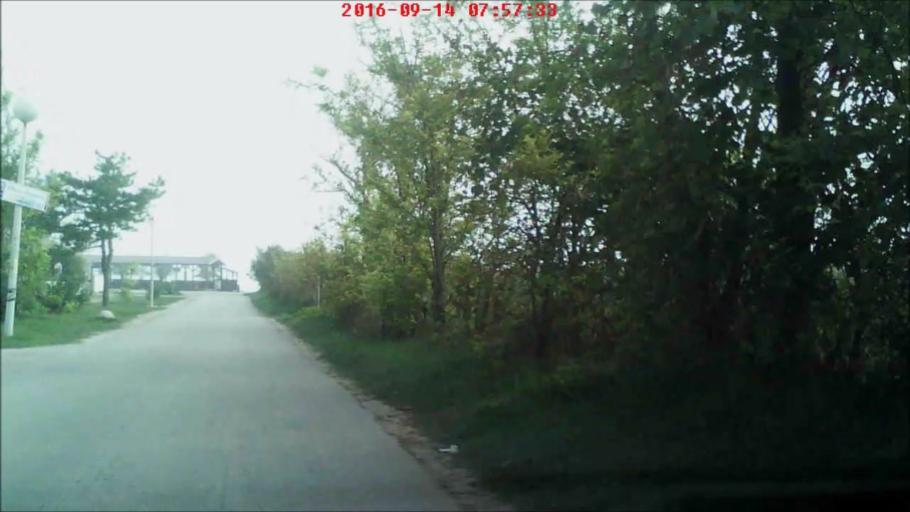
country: HR
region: Zadarska
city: Nin
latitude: 44.2582
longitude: 15.1636
